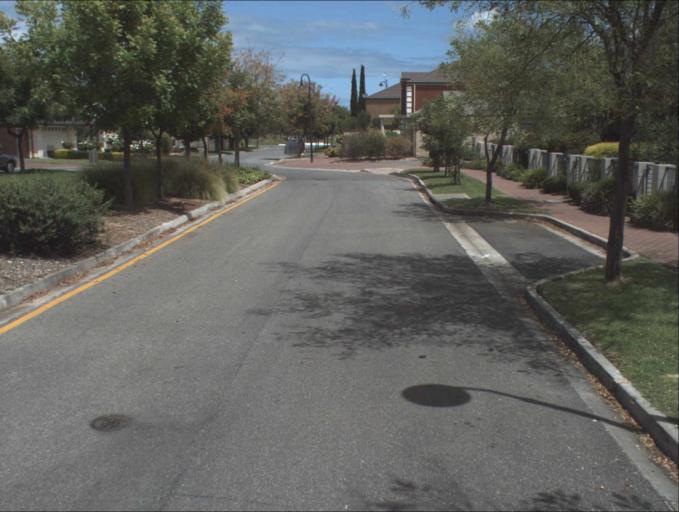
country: AU
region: South Australia
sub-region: Port Adelaide Enfield
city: Gilles Plains
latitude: -34.8540
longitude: 138.6301
